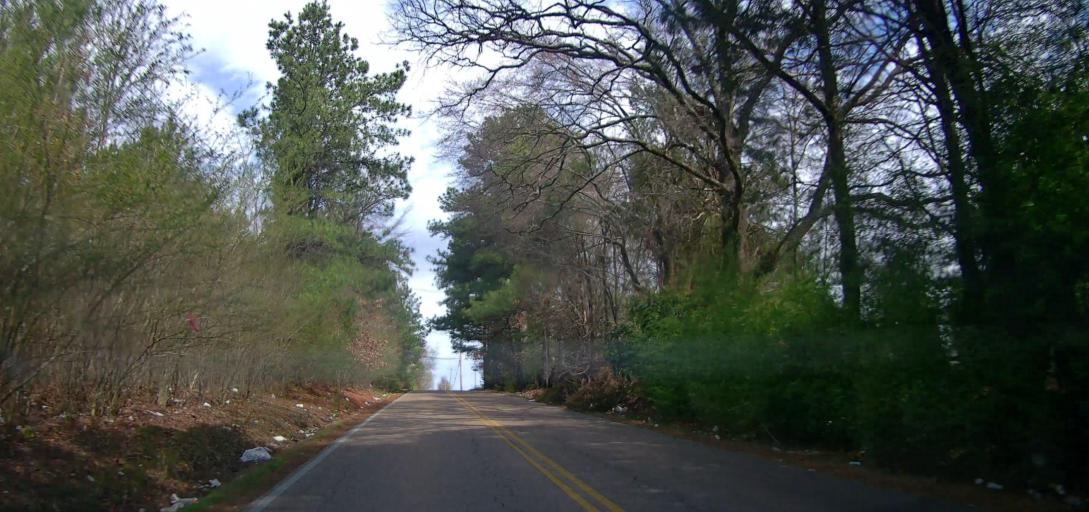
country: US
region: Mississippi
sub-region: De Soto County
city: Olive Branch
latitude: 34.9978
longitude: -89.8484
